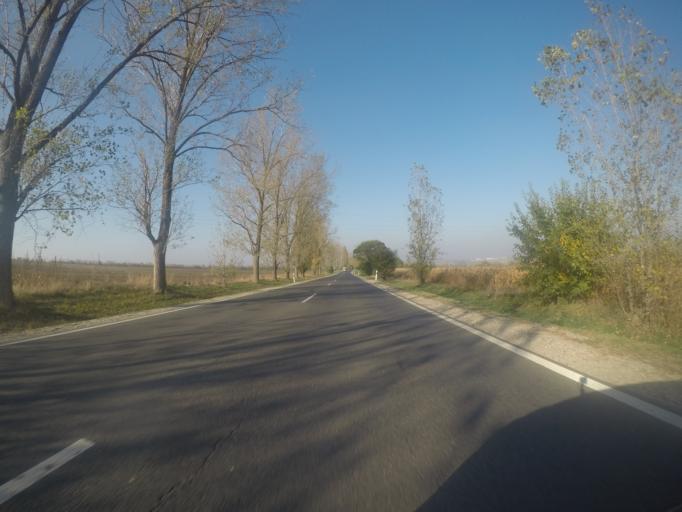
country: HU
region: Pest
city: Szazhalombatta
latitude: 47.3273
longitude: 18.8912
